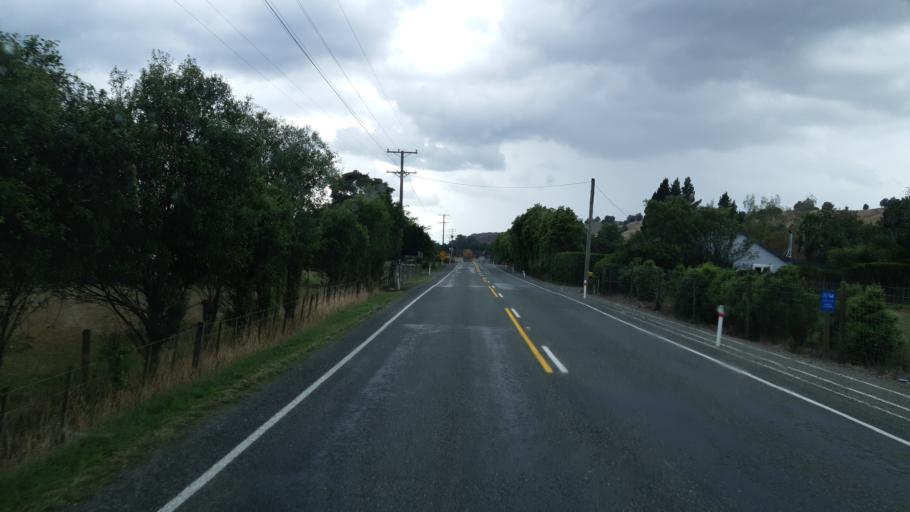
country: NZ
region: Tasman
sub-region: Tasman District
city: Wakefield
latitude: -41.4251
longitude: 172.9987
